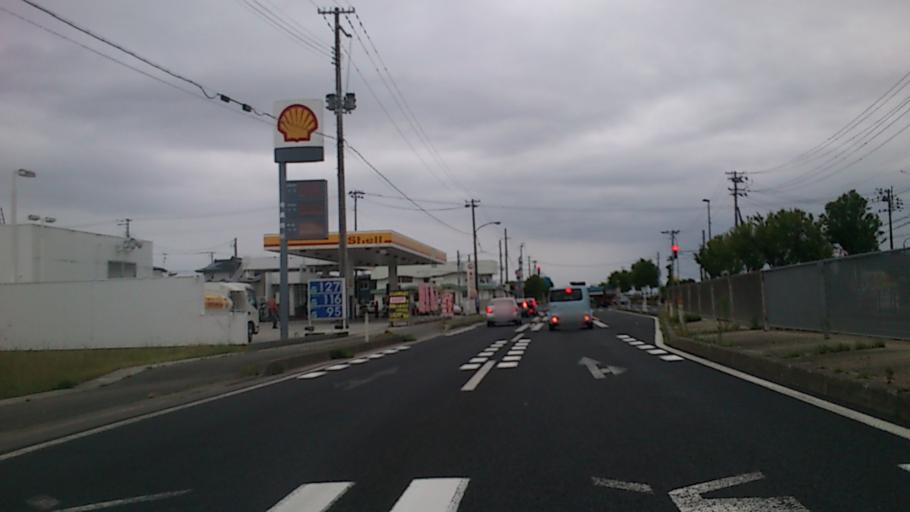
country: JP
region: Yamagata
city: Higashine
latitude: 38.4755
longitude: 140.3829
